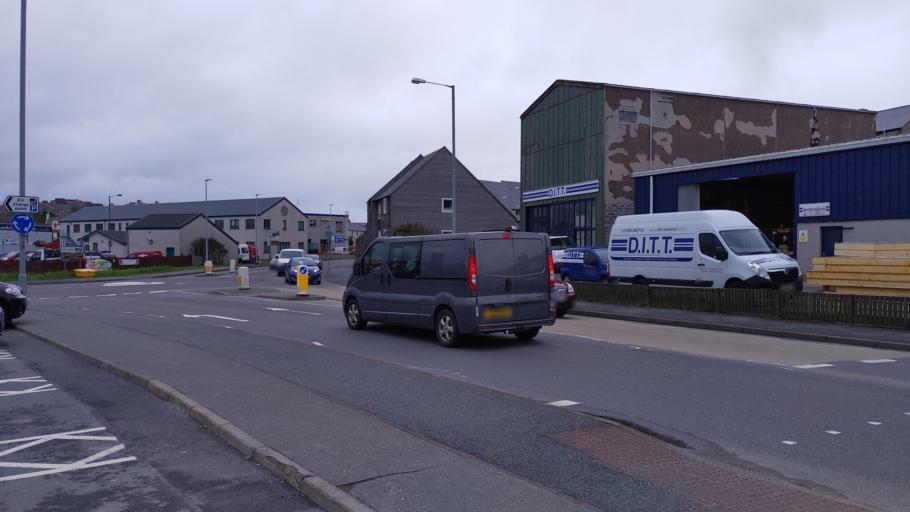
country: GB
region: Scotland
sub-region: Shetland Islands
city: Lerwick
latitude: 60.1594
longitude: -1.1569
